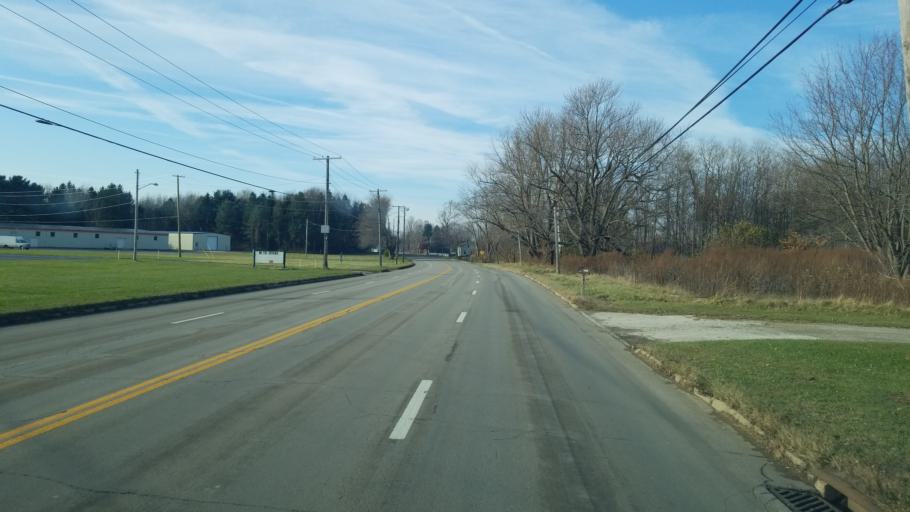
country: US
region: Ohio
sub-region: Ashtabula County
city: North Kingsville
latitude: 41.9165
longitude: -80.6694
